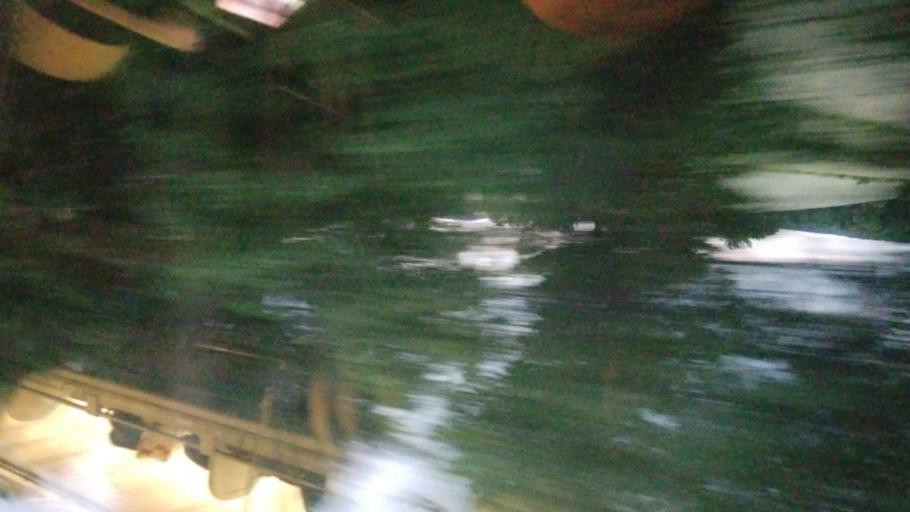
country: US
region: Virginia
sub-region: Orange County
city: Gordonsville
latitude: 38.2173
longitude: -78.2050
